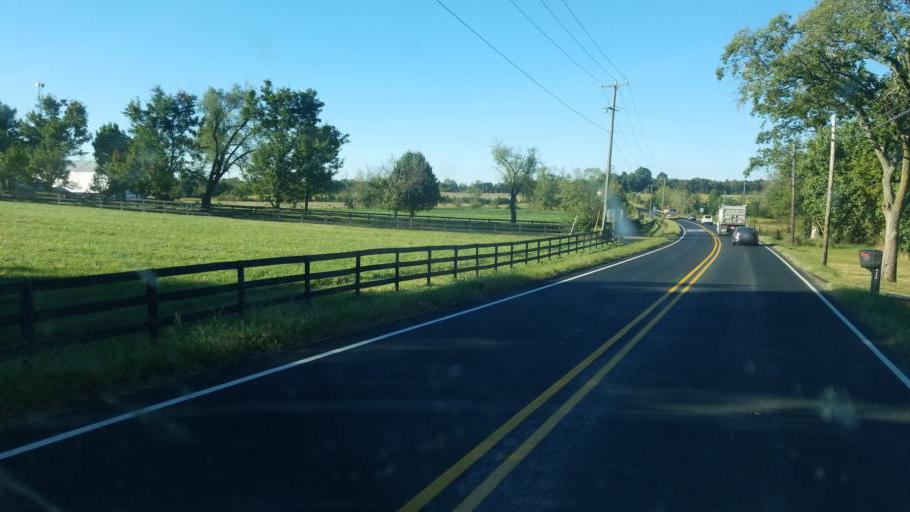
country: US
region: Virginia
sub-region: Fauquier County
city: Bealeton
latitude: 38.6348
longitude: -77.6763
